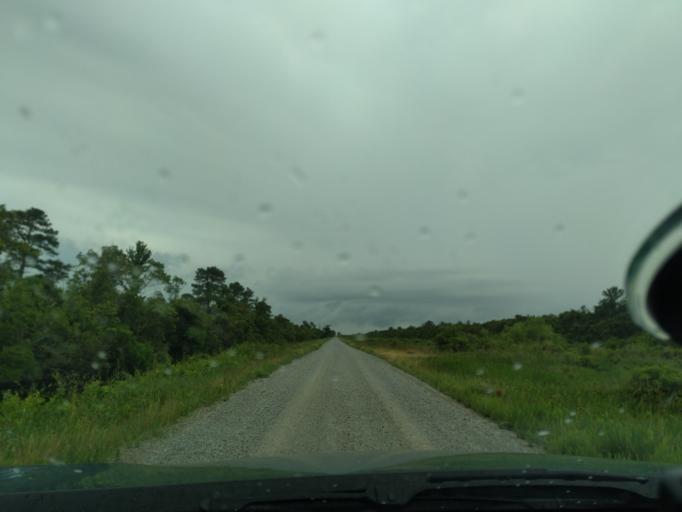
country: US
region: North Carolina
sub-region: Beaufort County
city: Belhaven
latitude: 35.7294
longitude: -76.4435
